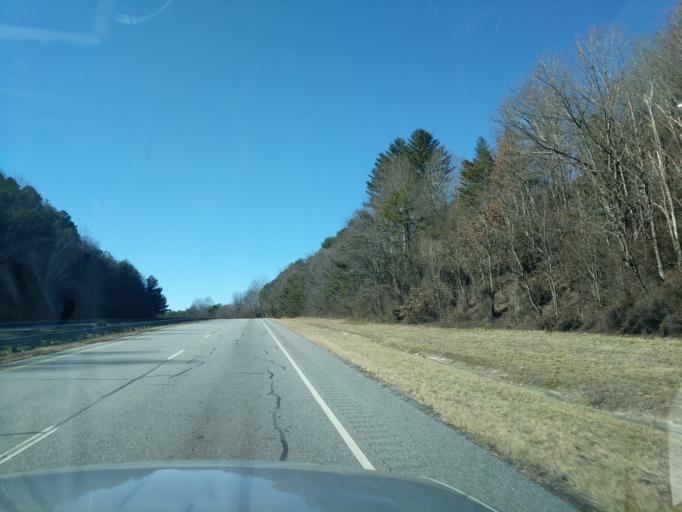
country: US
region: North Carolina
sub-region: Swain County
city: Bryson City
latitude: 35.4252
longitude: -83.4287
